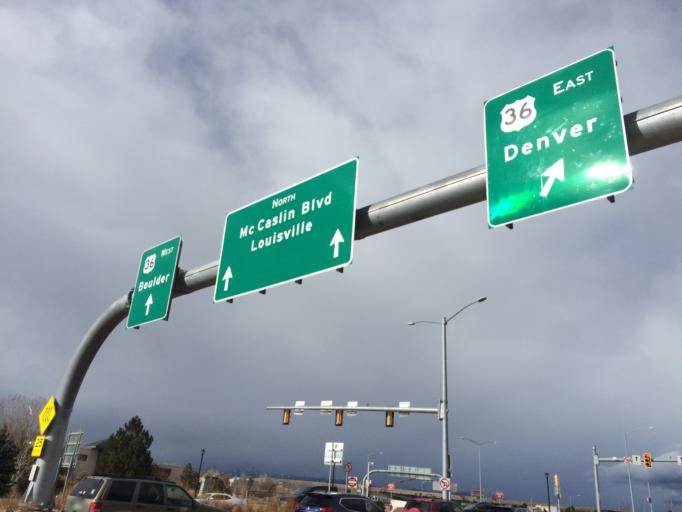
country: US
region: Colorado
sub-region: Boulder County
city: Superior
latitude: 39.9562
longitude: -105.1656
